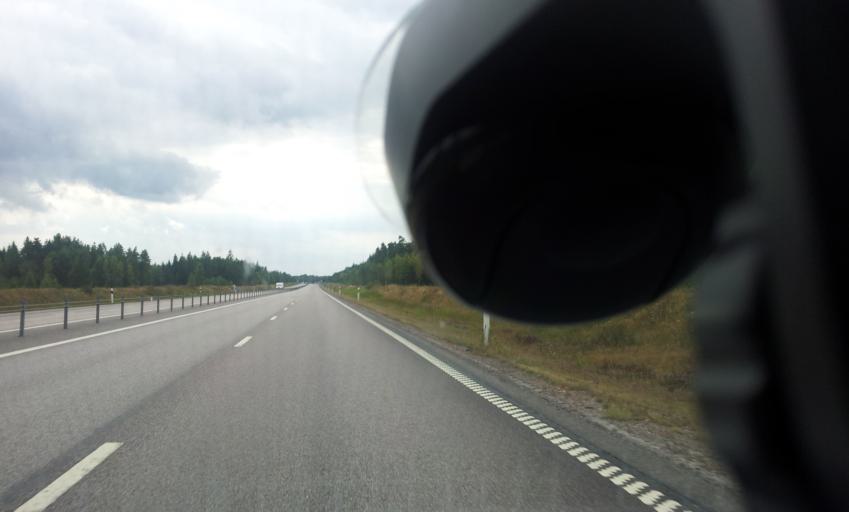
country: SE
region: Kalmar
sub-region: Monsteras Kommun
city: Timmernabben
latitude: 56.9790
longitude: 16.4017
